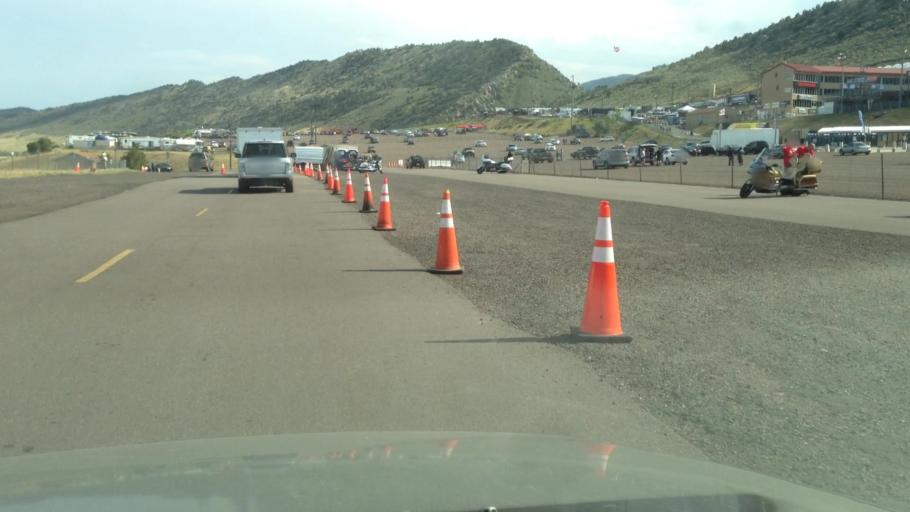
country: US
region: Colorado
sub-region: Jefferson County
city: Indian Hills
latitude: 39.6620
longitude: -105.1859
